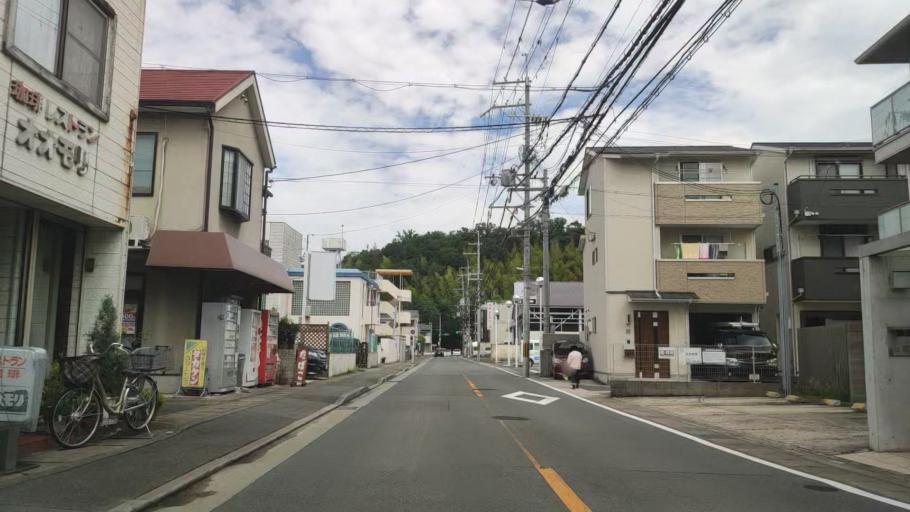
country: JP
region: Kyoto
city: Kyoto
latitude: 35.0221
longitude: 135.6981
